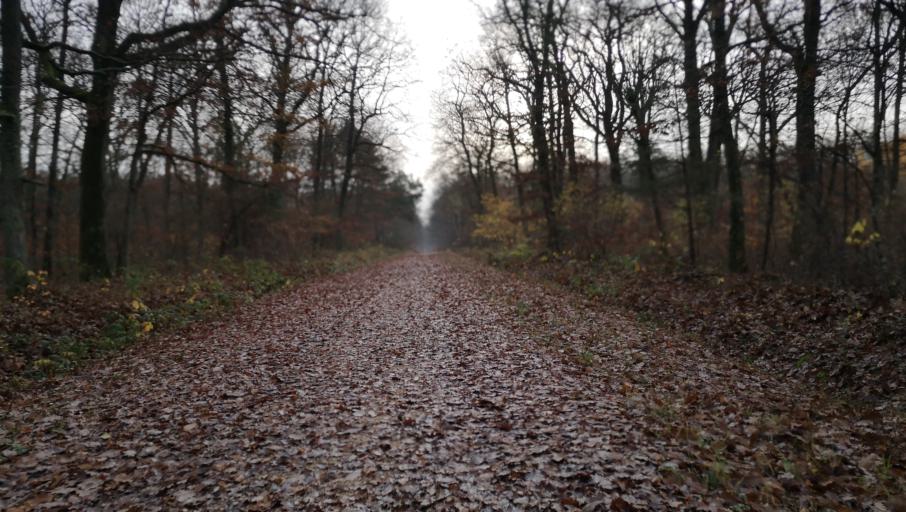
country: FR
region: Centre
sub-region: Departement du Loiret
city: Chanteau
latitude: 47.9454
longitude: 1.9685
